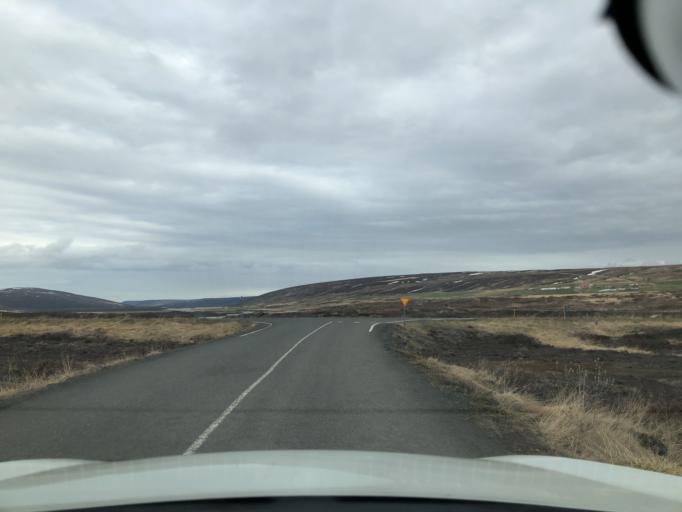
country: IS
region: Northeast
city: Laugar
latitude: 65.6864
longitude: -17.5459
